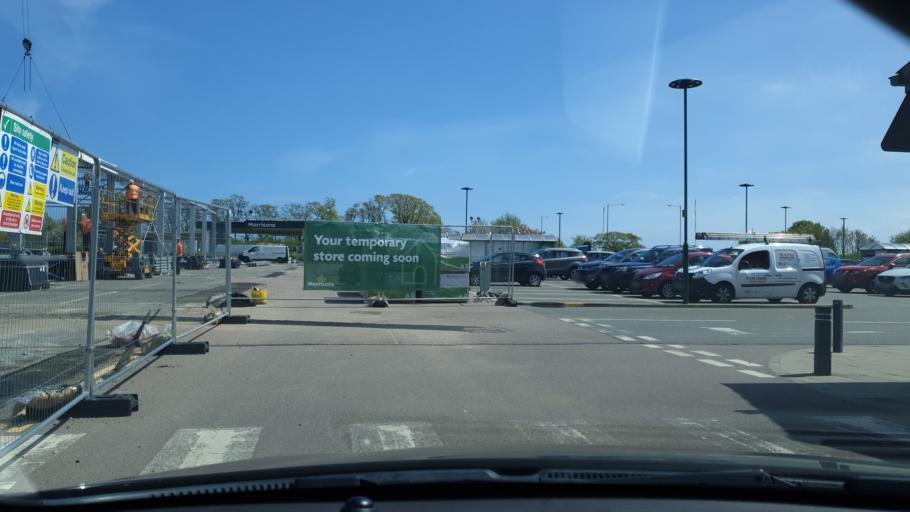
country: GB
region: England
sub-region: Essex
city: Little Clacton
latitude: 51.8204
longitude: 1.1499
